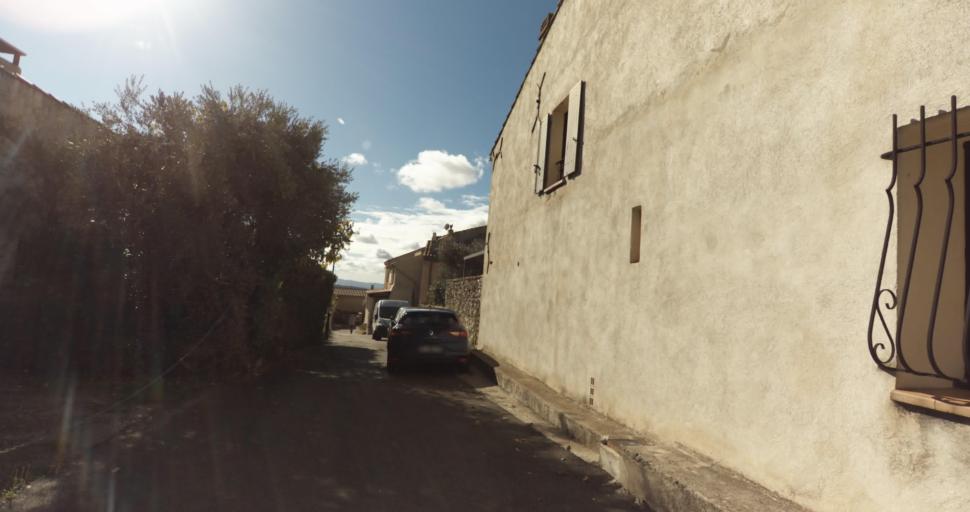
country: FR
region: Provence-Alpes-Cote d'Azur
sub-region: Departement des Bouches-du-Rhone
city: Venelles
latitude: 43.5999
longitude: 5.4810
